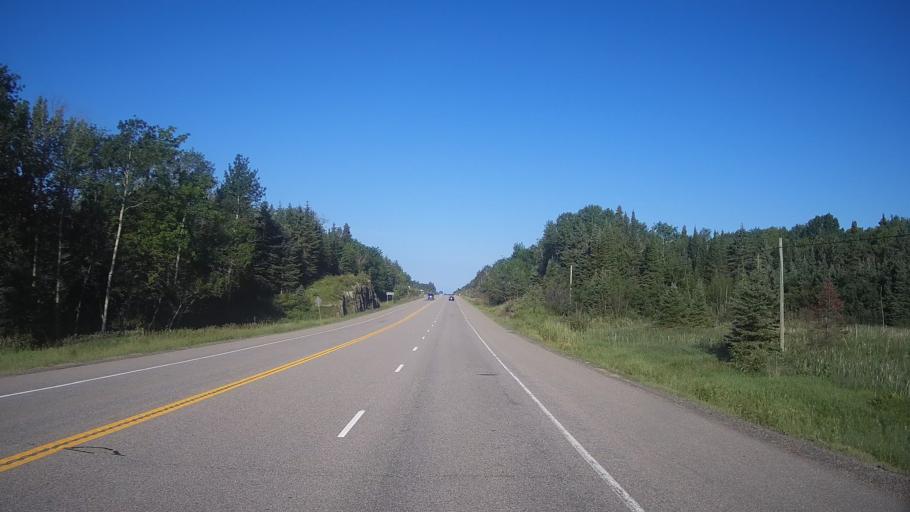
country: US
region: Minnesota
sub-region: Roseau County
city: Warroad
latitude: 49.7187
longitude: -94.7321
